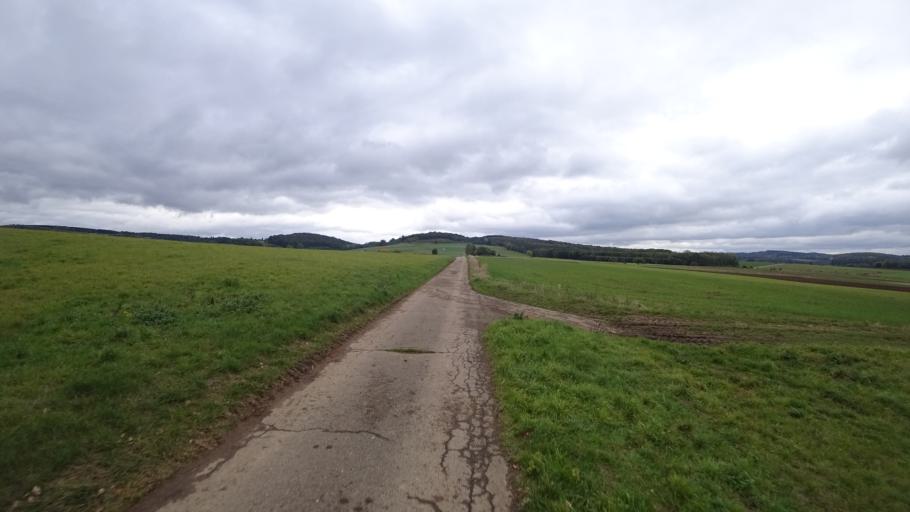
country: DE
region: Rheinland-Pfalz
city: Maxsain
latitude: 50.5626
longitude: 7.7738
